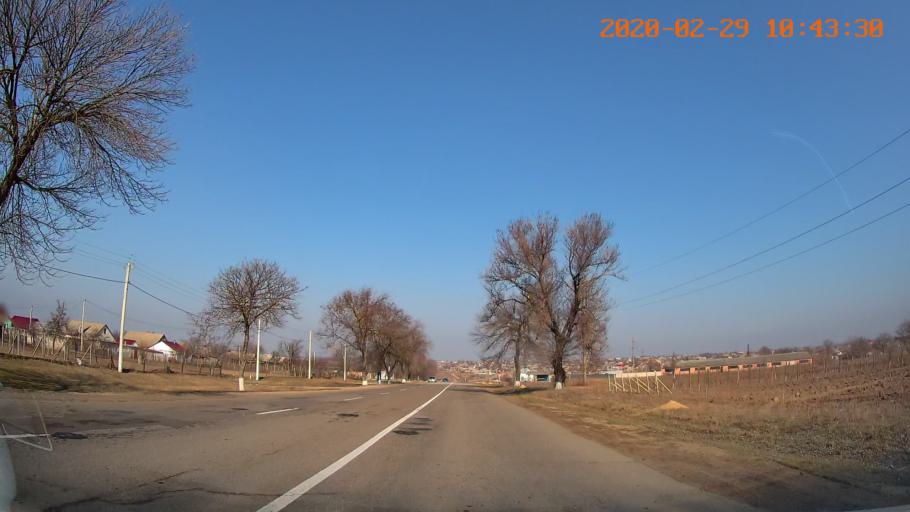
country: MD
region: Telenesti
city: Grigoriopol
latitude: 47.0620
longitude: 29.4032
